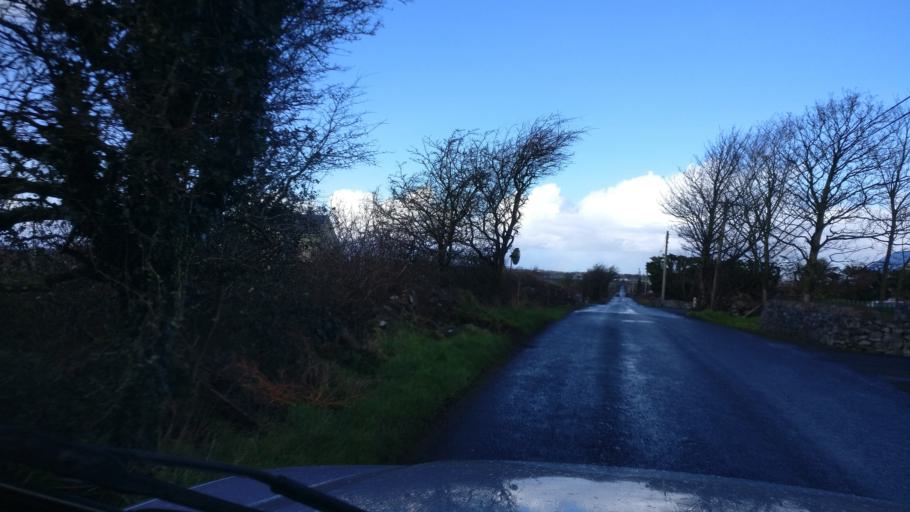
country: IE
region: Connaught
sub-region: County Galway
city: Oranmore
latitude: 53.2620
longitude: -8.8646
